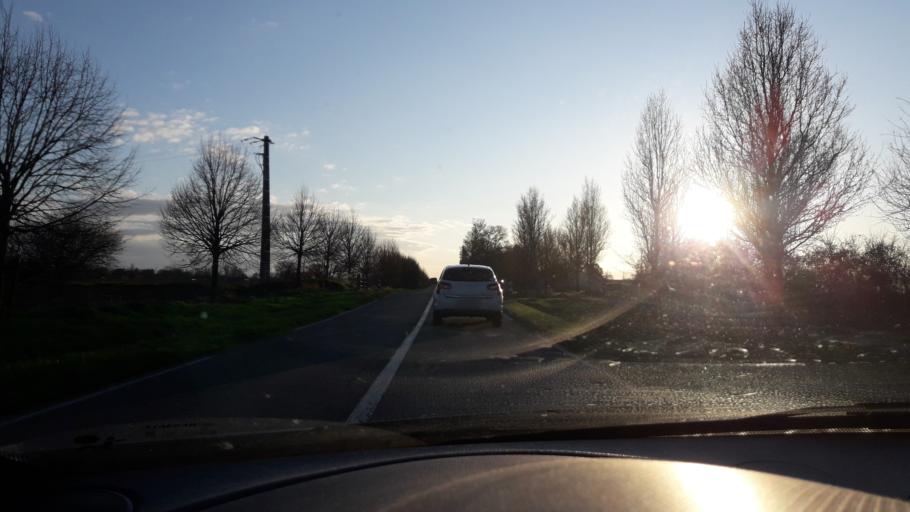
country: FR
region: Midi-Pyrenees
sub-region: Departement de la Haute-Garonne
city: Levignac
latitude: 43.6517
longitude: 1.1732
